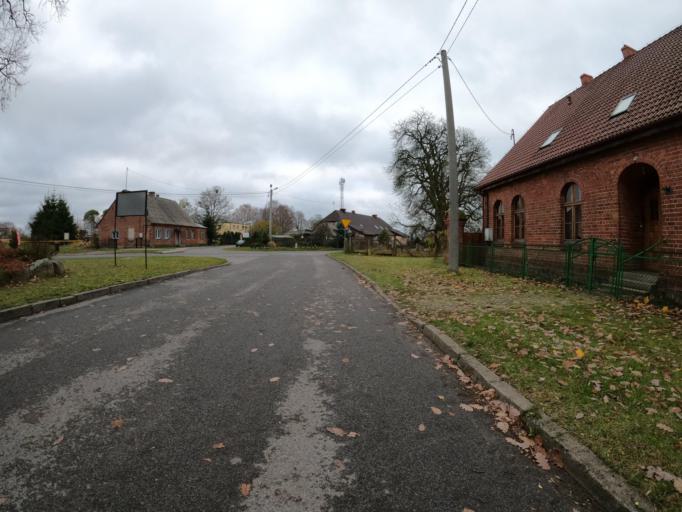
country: PL
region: West Pomeranian Voivodeship
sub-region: Powiat walecki
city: Tuczno
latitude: 53.2666
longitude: 16.1857
